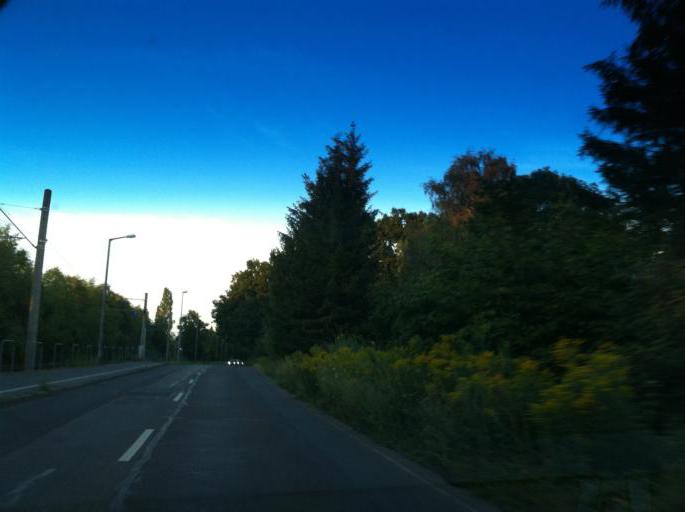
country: DE
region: Saxony
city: Markkleeberg
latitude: 51.2885
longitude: 12.3163
